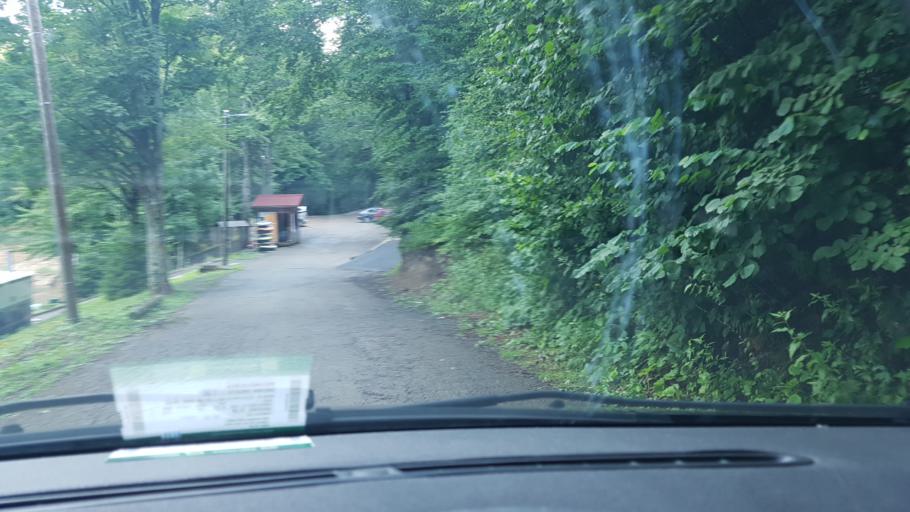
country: HR
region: Primorsko-Goranska
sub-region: Grad Delnice
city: Delnice
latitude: 45.3616
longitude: 14.7192
